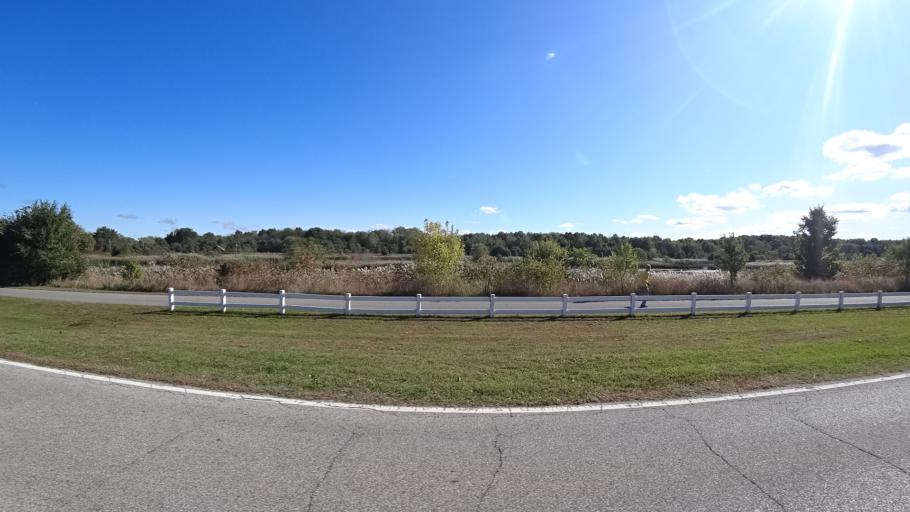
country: US
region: Indiana
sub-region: LaPorte County
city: Michigan City
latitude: 41.6892
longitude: -86.9132
